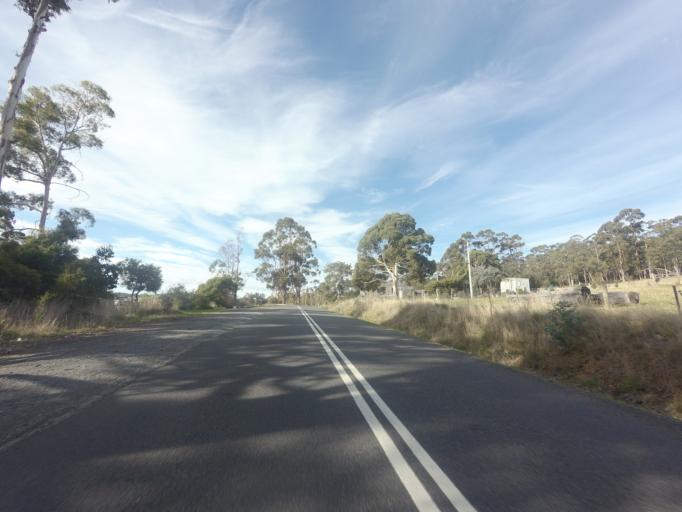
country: AU
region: Tasmania
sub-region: Clarence
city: Sandford
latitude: -43.0616
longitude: 147.8251
